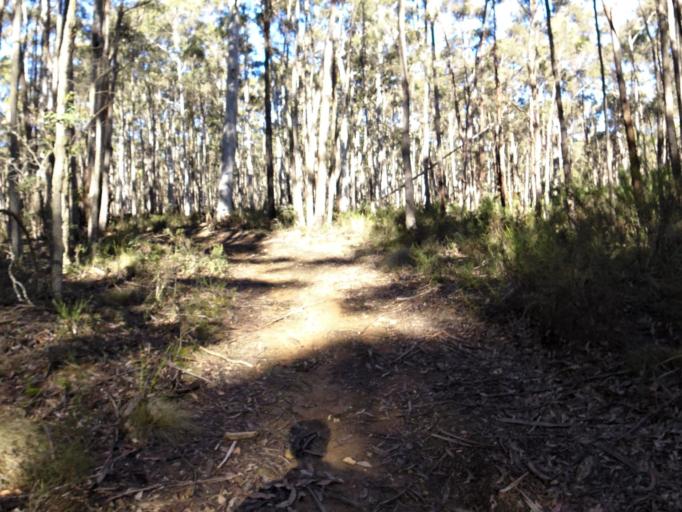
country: AU
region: Victoria
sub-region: Moorabool
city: Bacchus Marsh
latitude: -37.3937
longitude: 144.2842
